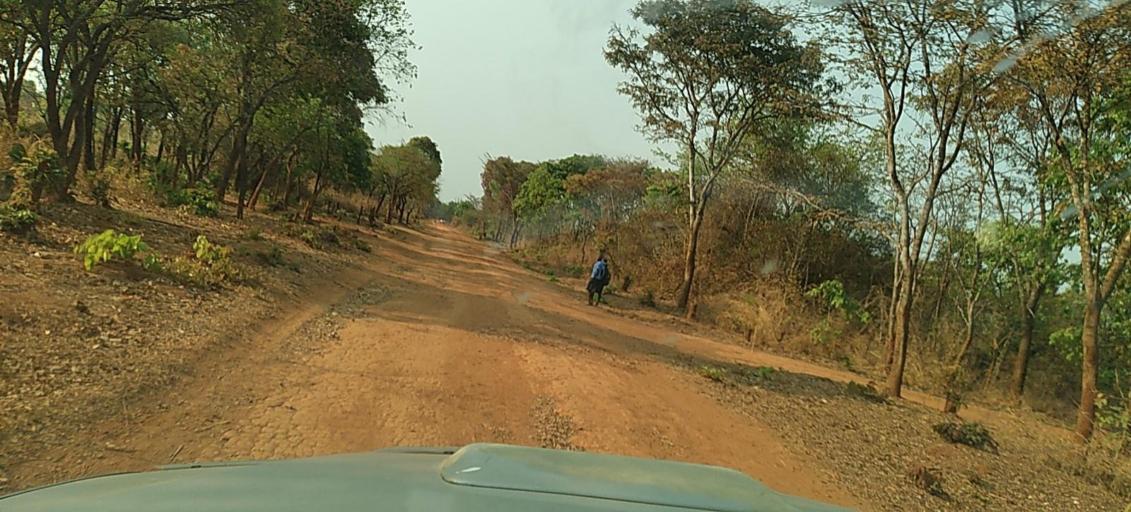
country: ZM
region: North-Western
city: Kasempa
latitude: -13.2987
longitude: 26.5542
